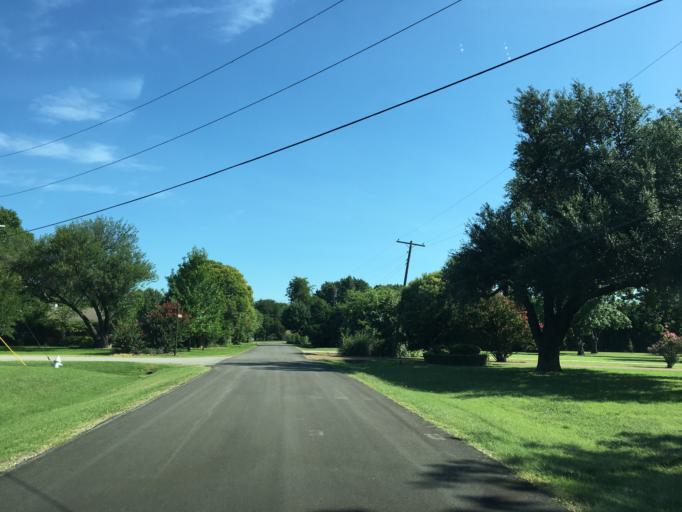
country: US
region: Texas
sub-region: Dallas County
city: Farmers Branch
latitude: 32.9226
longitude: -96.8692
